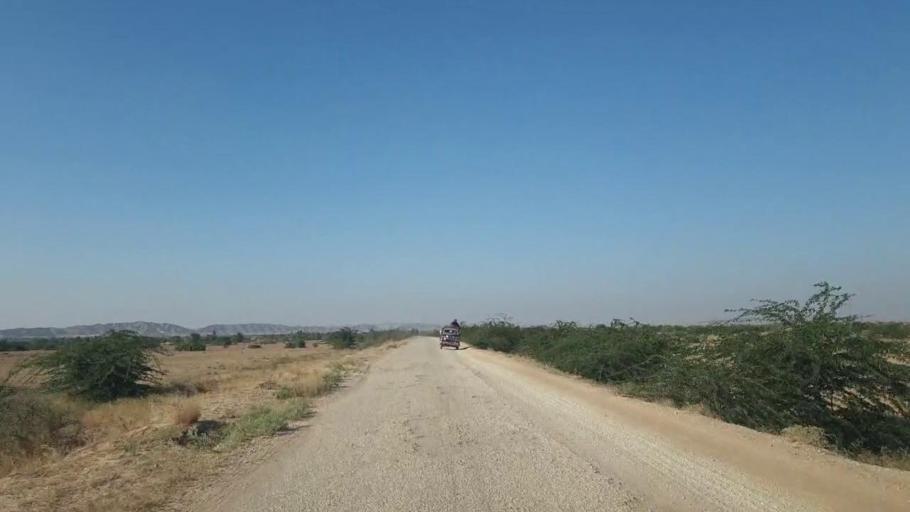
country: PK
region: Sindh
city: Malir Cantonment
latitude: 25.3353
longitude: 67.5715
